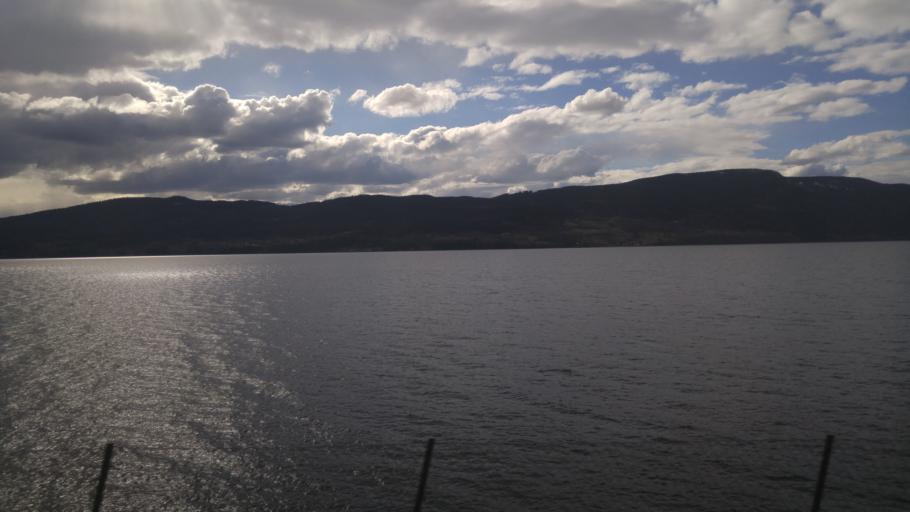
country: NO
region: Hedmark
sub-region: Stange
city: Stange
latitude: 60.5482
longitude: 11.2461
